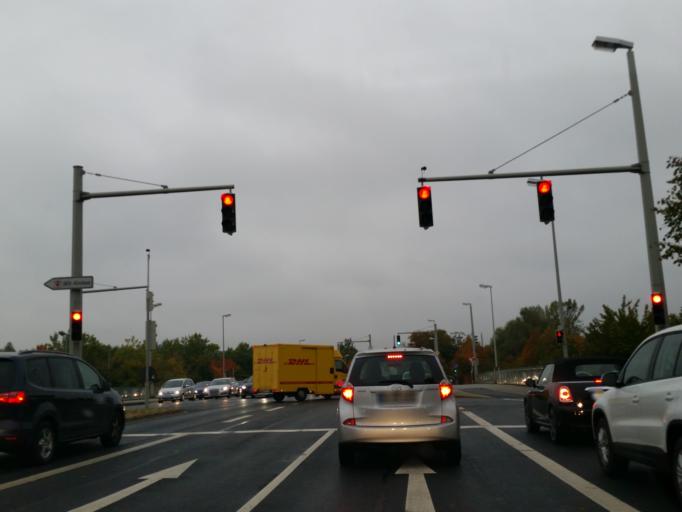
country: DE
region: Lower Saxony
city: Braunschweig
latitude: 52.2387
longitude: 10.5411
